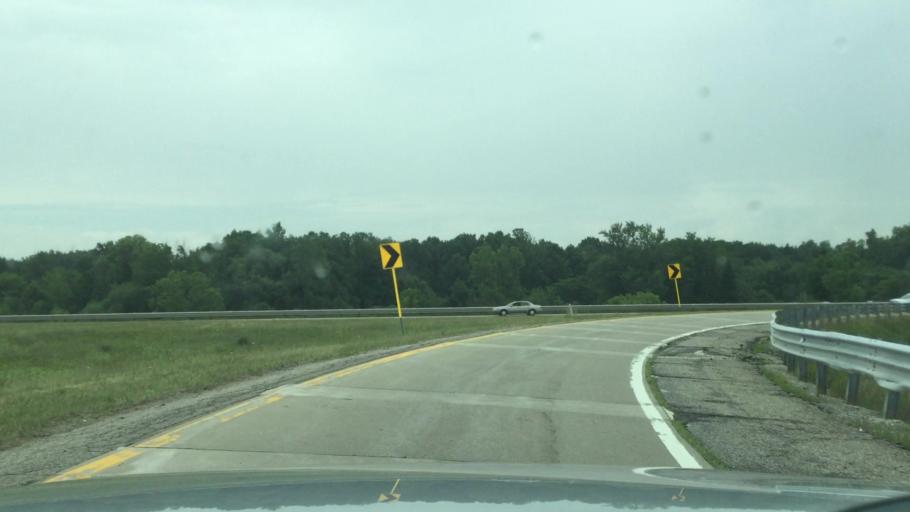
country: US
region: Michigan
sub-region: Genesee County
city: Swartz Creek
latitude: 42.9649
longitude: -83.8052
